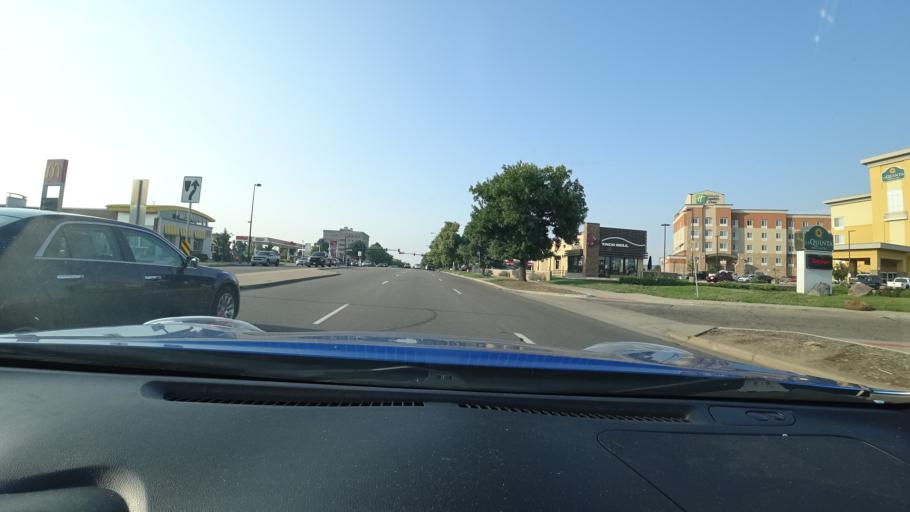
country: US
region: Colorado
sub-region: Adams County
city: Aurora
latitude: 39.7765
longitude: -104.8469
